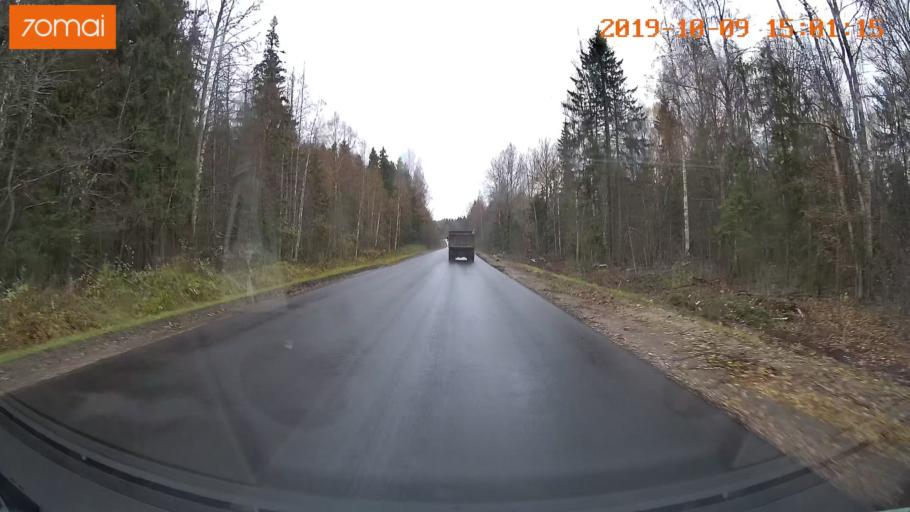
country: RU
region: Kostroma
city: Chistyye Bory
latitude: 58.2987
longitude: 41.6802
